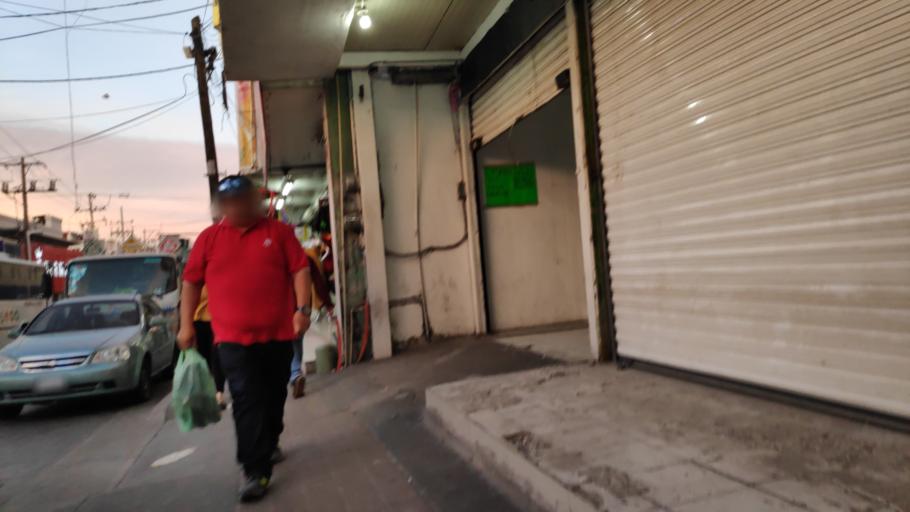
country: MX
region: Sinaloa
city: Culiacan
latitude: 24.8059
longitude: -107.3962
